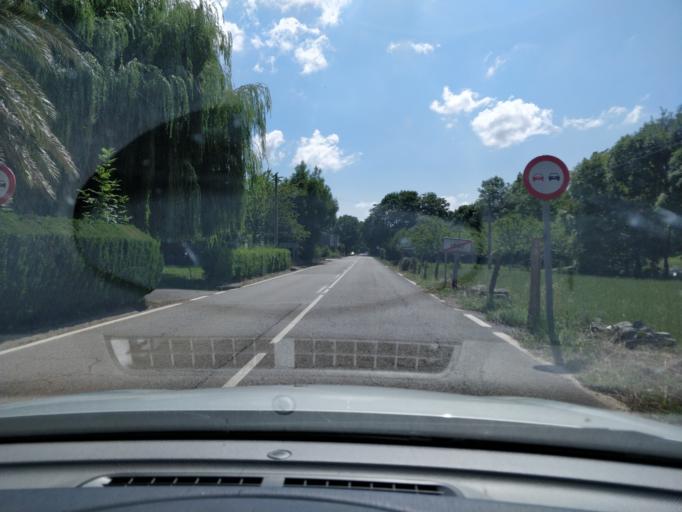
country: ES
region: Cantabria
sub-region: Provincia de Cantabria
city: Corvera
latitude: 43.2689
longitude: -3.9234
